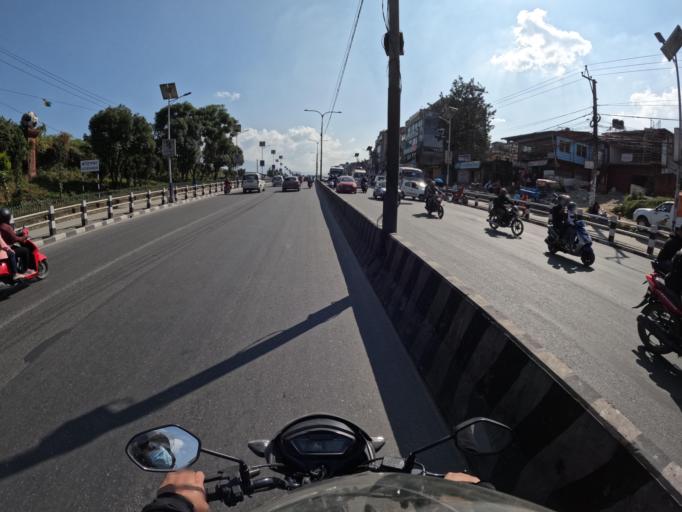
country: NP
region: Central Region
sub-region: Bagmati Zone
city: Kathmandu
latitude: 27.6813
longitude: 85.3503
